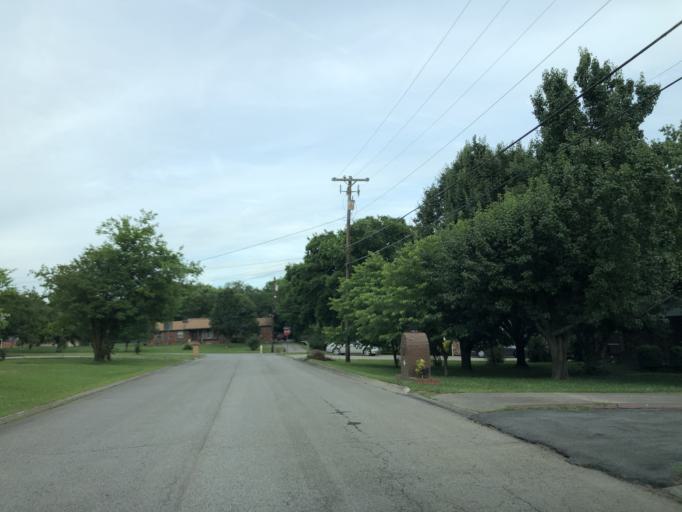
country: US
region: Tennessee
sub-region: Davidson County
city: Goodlettsville
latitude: 36.2942
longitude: -86.7109
